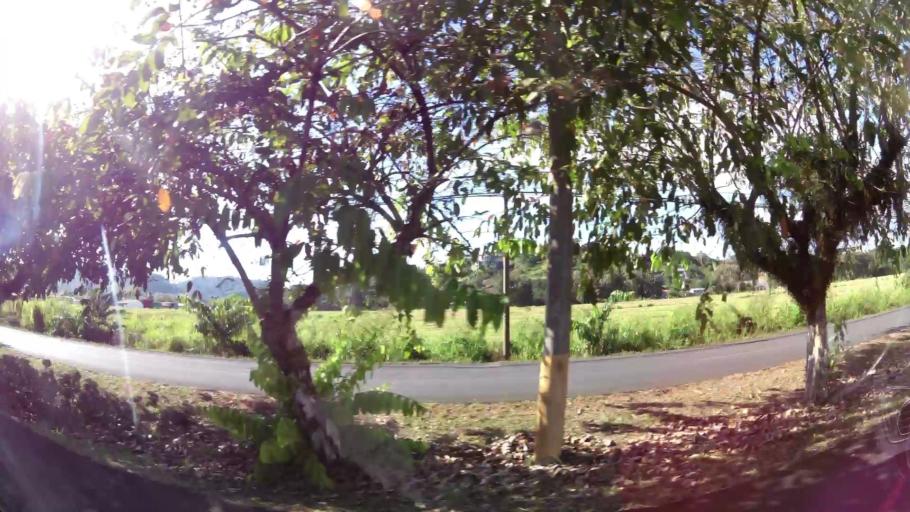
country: CR
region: Puntarenas
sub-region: Canton de Garabito
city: Jaco
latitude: 9.6300
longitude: -84.6314
